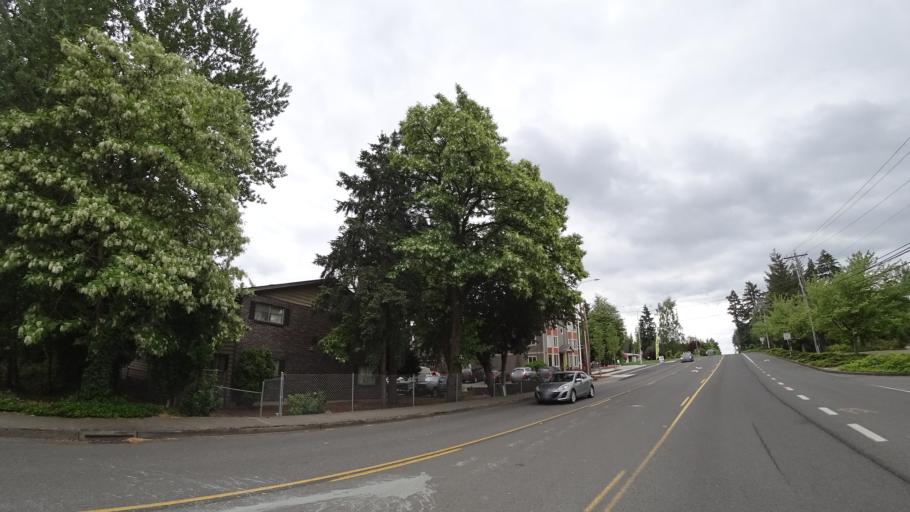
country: US
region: Oregon
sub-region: Washington County
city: Metzger
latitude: 45.4515
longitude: -122.7744
